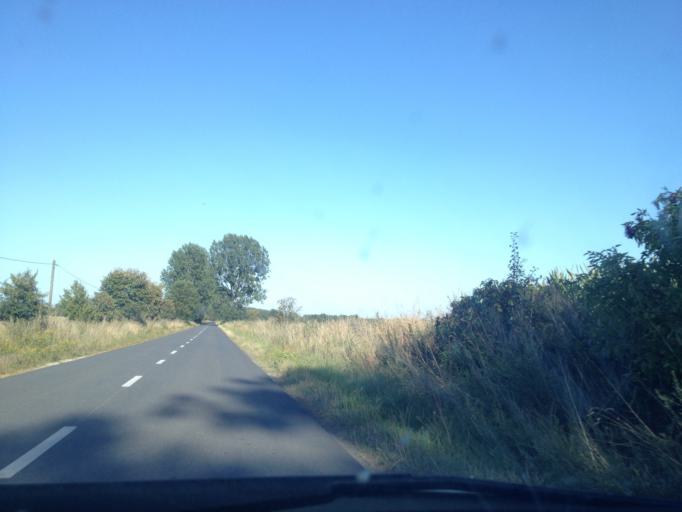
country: PL
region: Greater Poland Voivodeship
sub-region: Powiat sremski
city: Srem
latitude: 52.1107
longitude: 17.0775
